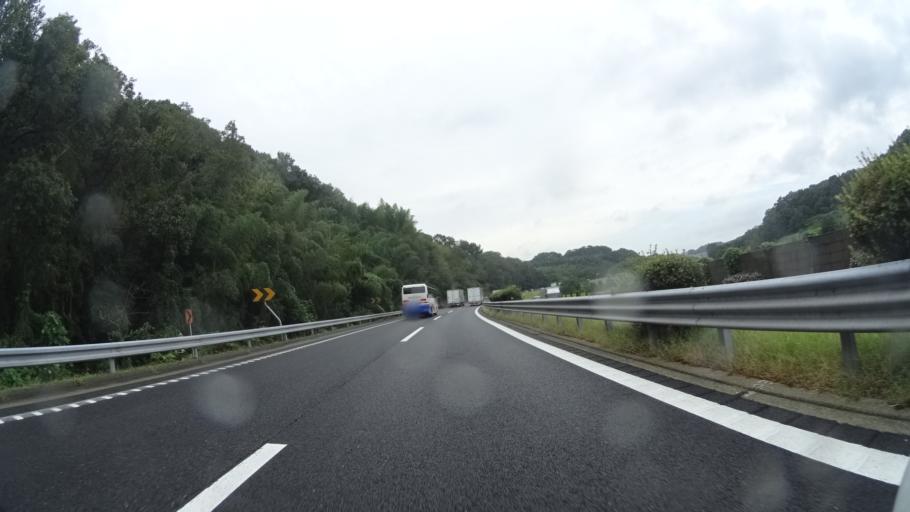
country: JP
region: Hyogo
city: Sandacho
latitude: 34.8897
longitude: 135.1359
